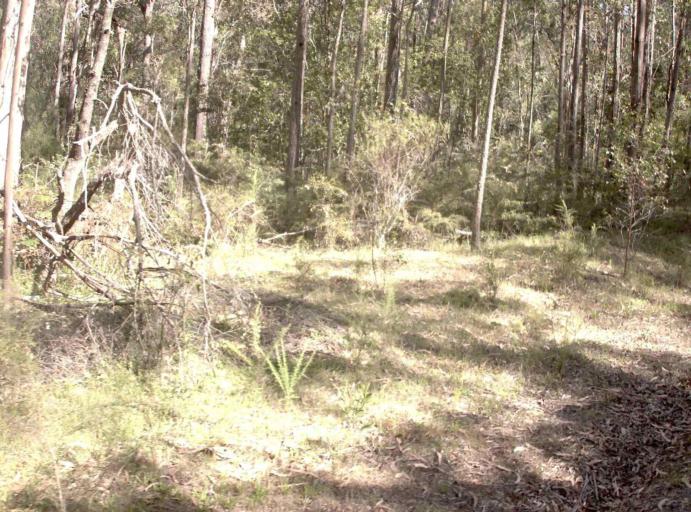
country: AU
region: New South Wales
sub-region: Bombala
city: Bombala
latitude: -37.2915
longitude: 148.7123
